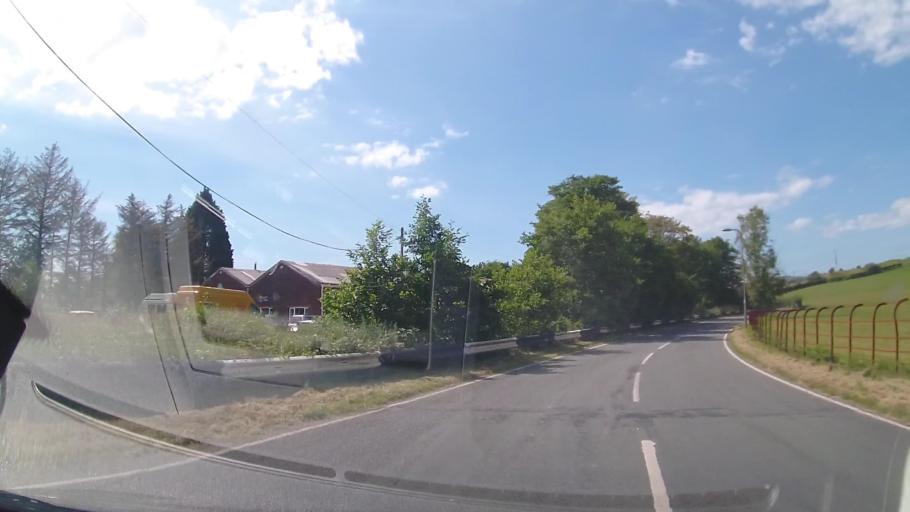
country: GB
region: Wales
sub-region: Gwynedd
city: Tywyn
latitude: 52.6083
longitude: -4.0482
